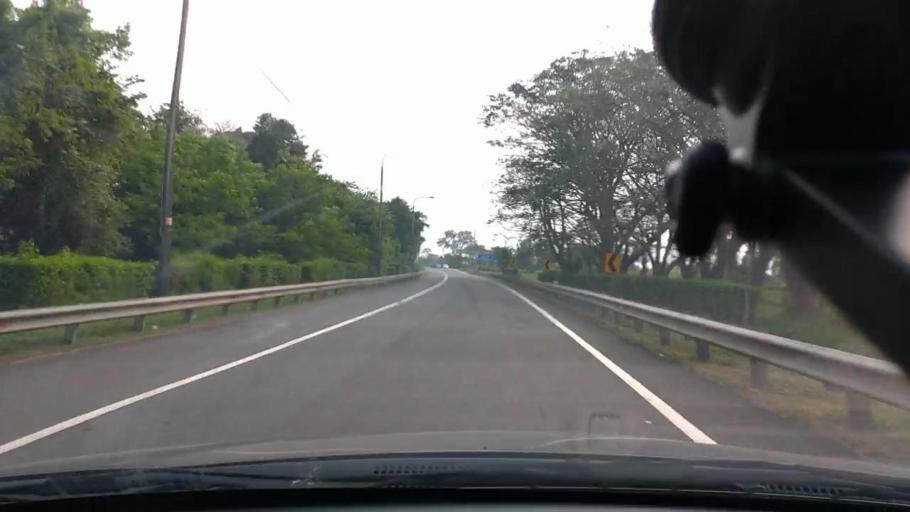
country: ID
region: Banten
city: Serang
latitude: -6.0895
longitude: 106.1457
